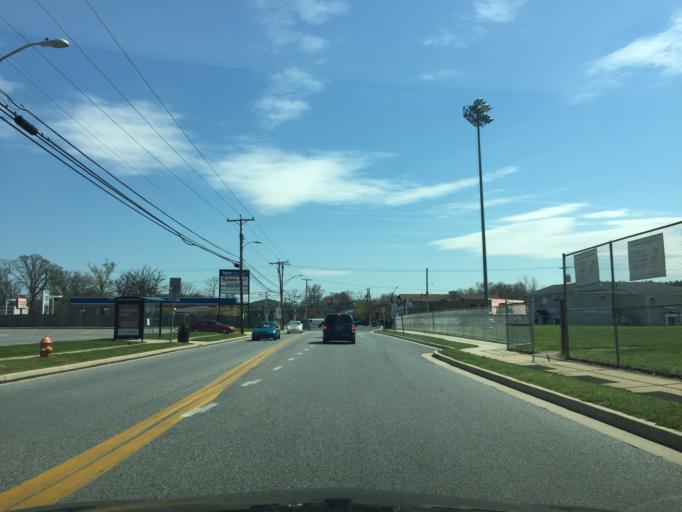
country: US
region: Maryland
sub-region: Baltimore County
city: Middle River
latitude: 39.3212
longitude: -76.4556
